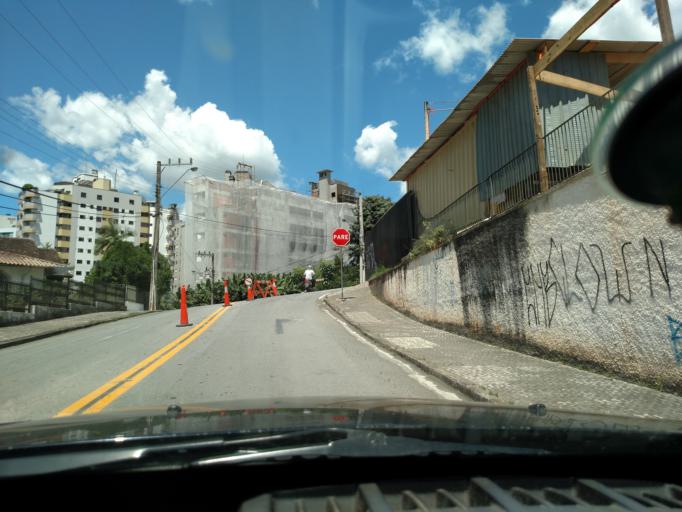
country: BR
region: Santa Catarina
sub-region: Blumenau
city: Blumenau
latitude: -26.9293
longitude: -49.0651
